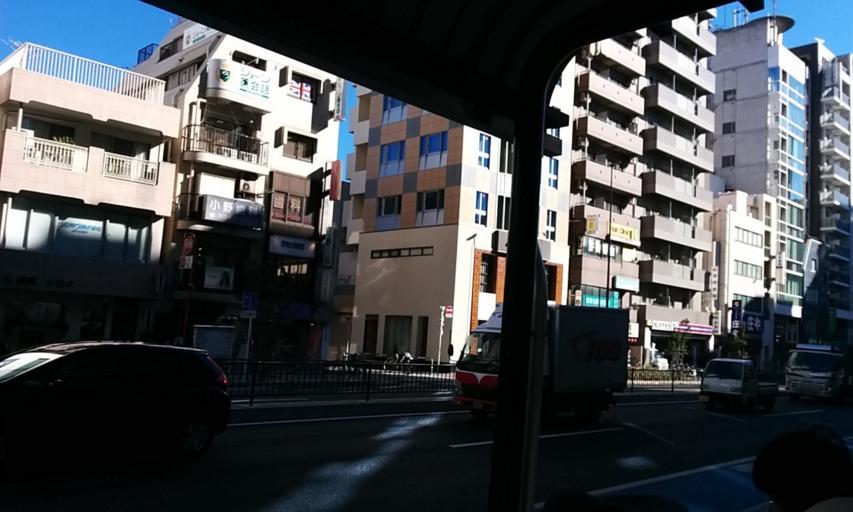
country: JP
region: Tokyo
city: Tokyo
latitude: 35.7174
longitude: 139.7373
